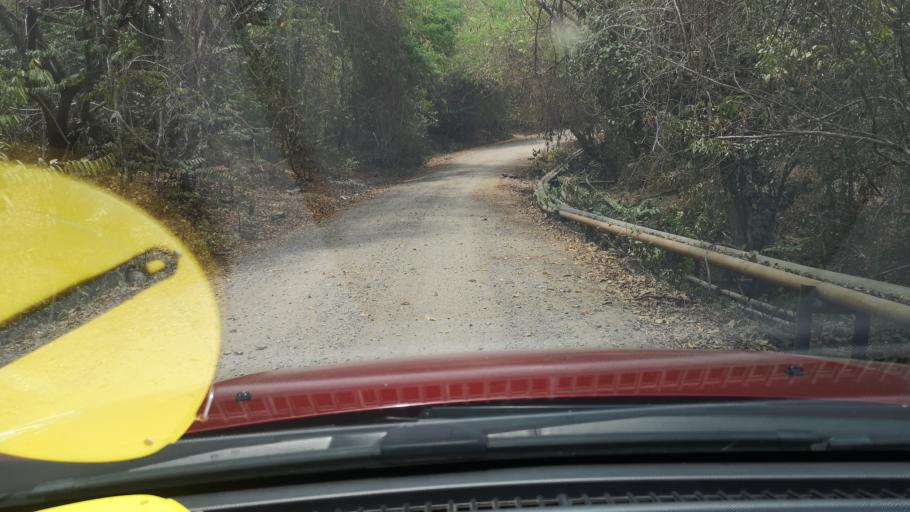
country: CO
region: Huila
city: Neiva
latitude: 2.9569
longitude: -75.3377
